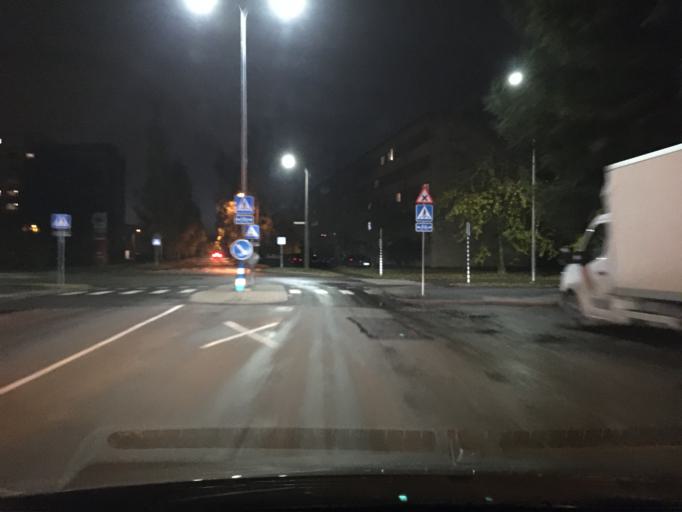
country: EE
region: Tartu
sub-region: Tartu linn
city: Tartu
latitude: 58.3785
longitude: 26.6838
